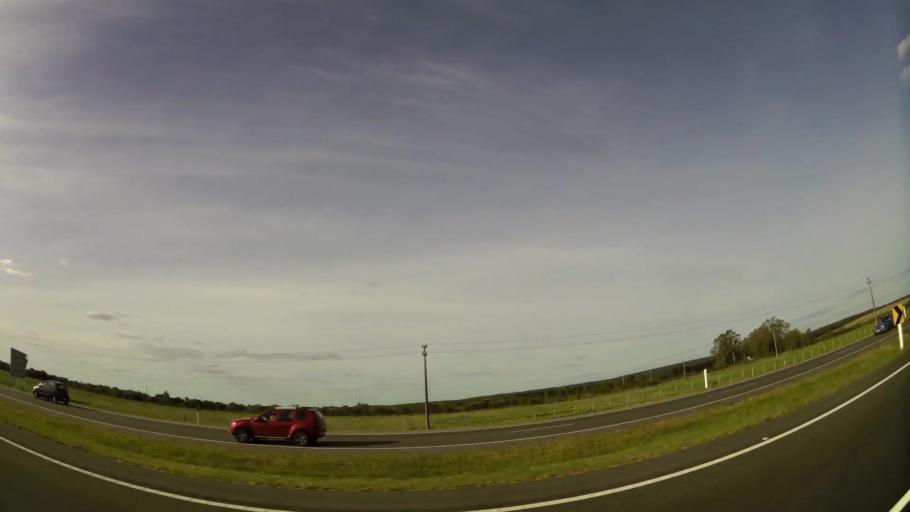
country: UY
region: Canelones
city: La Floresta
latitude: -34.7545
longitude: -55.6009
